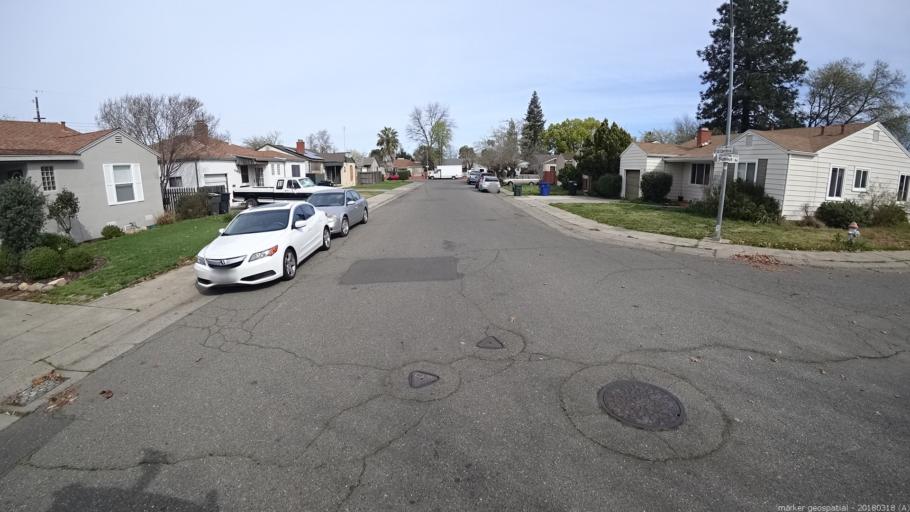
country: US
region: California
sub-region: Sacramento County
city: Parkway
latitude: 38.5369
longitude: -121.4538
